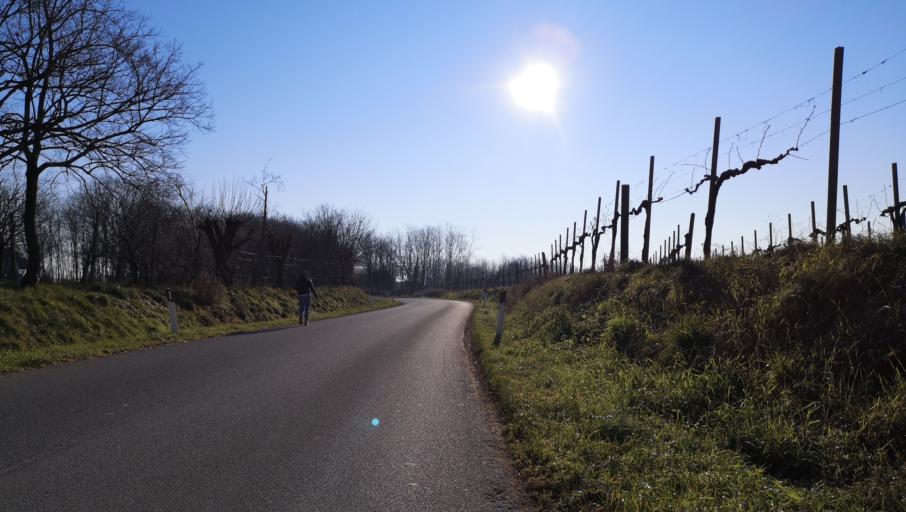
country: IT
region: Friuli Venezia Giulia
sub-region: Provincia di Udine
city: Bicinicco
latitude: 45.9529
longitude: 13.2677
